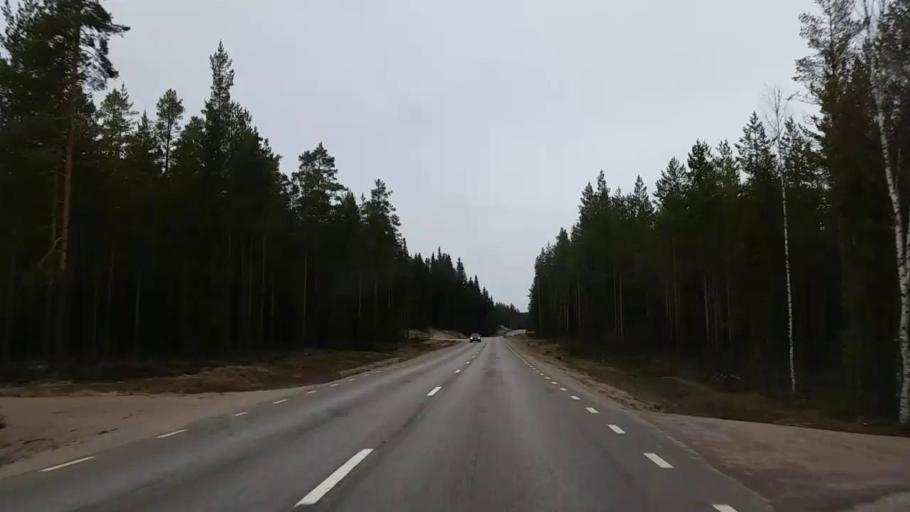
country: SE
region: Gaevleborg
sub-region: Ovanakers Kommun
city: Edsbyn
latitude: 61.1660
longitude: 15.8824
